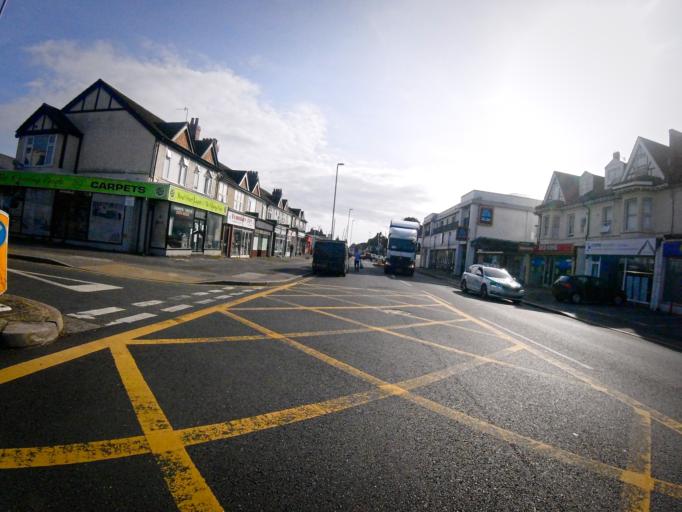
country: GB
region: England
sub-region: East Sussex
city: Portslade
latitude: 50.8365
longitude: -0.2053
